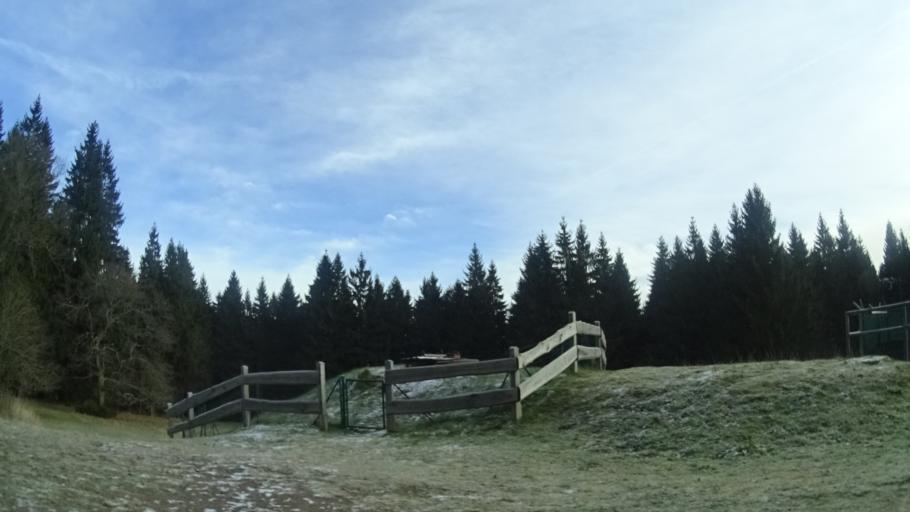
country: DE
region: Thuringia
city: Friedrichroda
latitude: 50.8288
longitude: 10.5440
